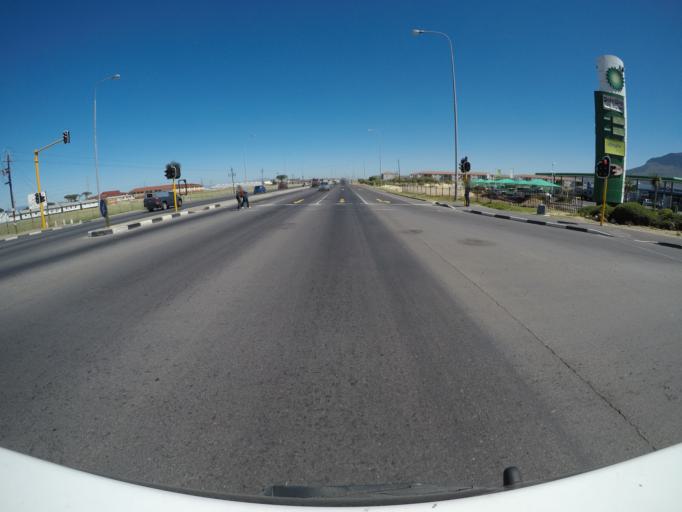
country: ZA
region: Western Cape
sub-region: Overberg District Municipality
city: Grabouw
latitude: -34.1081
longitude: 18.8610
